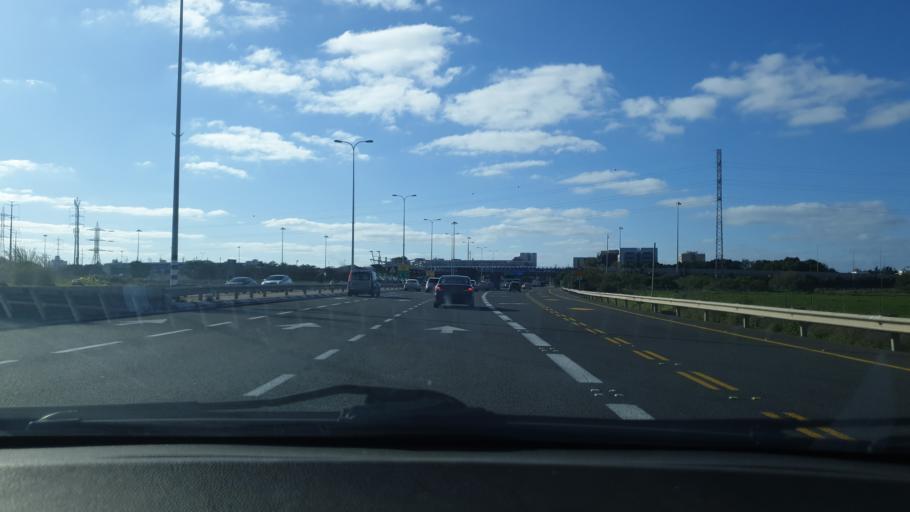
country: IL
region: Tel Aviv
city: Holon
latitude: 32.0368
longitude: 34.7818
